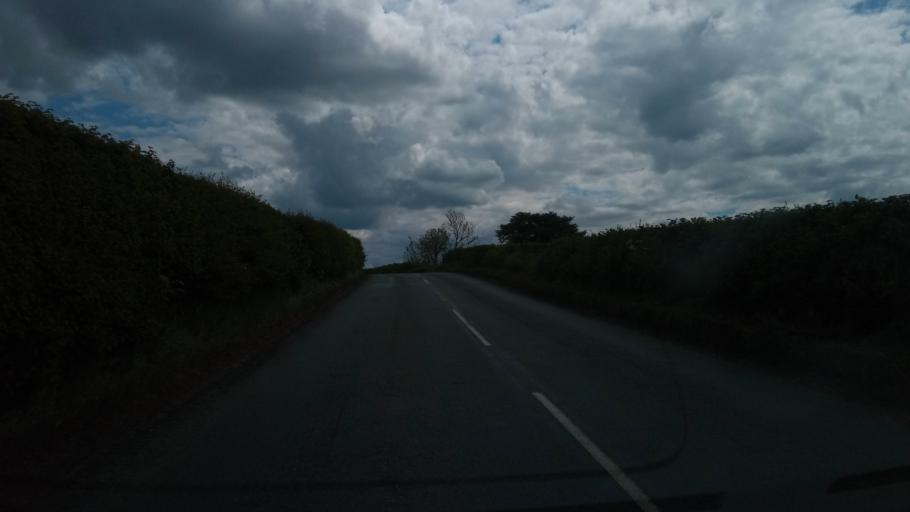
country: GB
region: Scotland
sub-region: The Scottish Borders
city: Kelso
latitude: 55.5832
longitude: -2.4170
